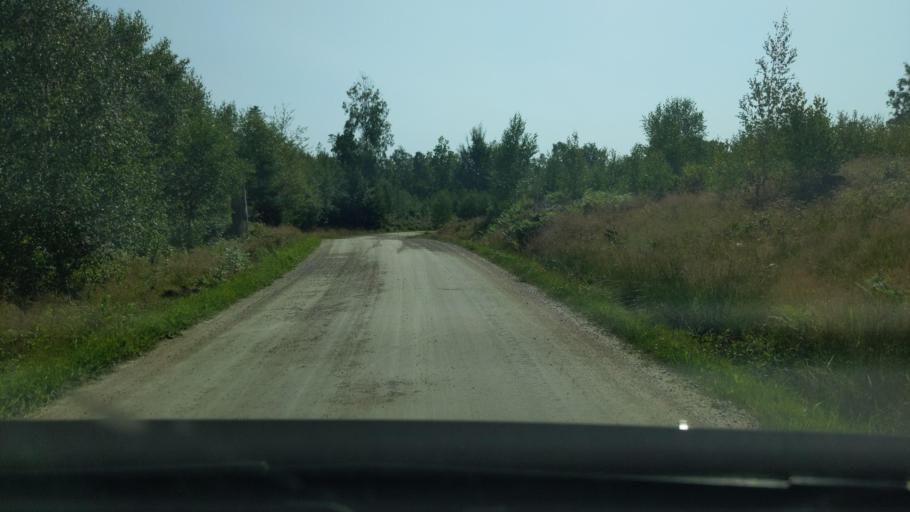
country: SE
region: Vaestra Goetaland
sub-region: Uddevalla Kommun
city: Uddevalla
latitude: 58.3420
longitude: 11.8133
